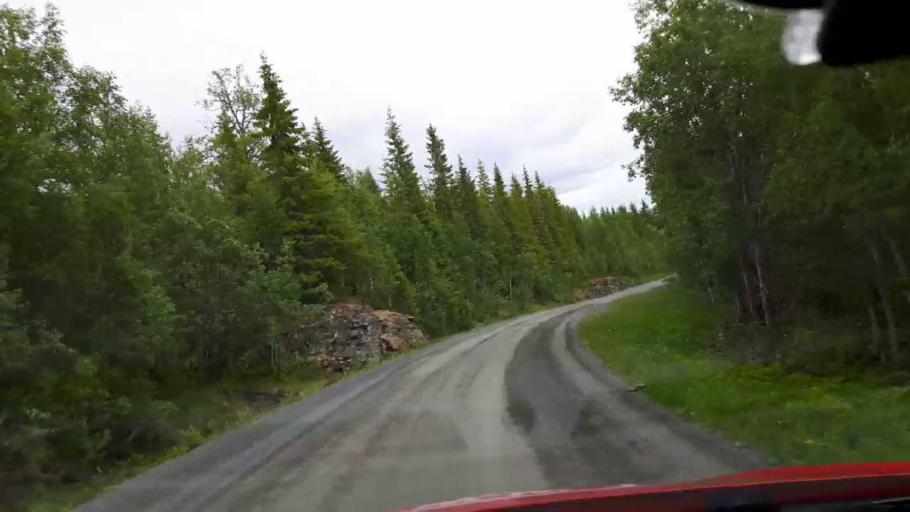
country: NO
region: Nord-Trondelag
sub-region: Lierne
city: Sandvika
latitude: 64.1554
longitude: 13.9912
